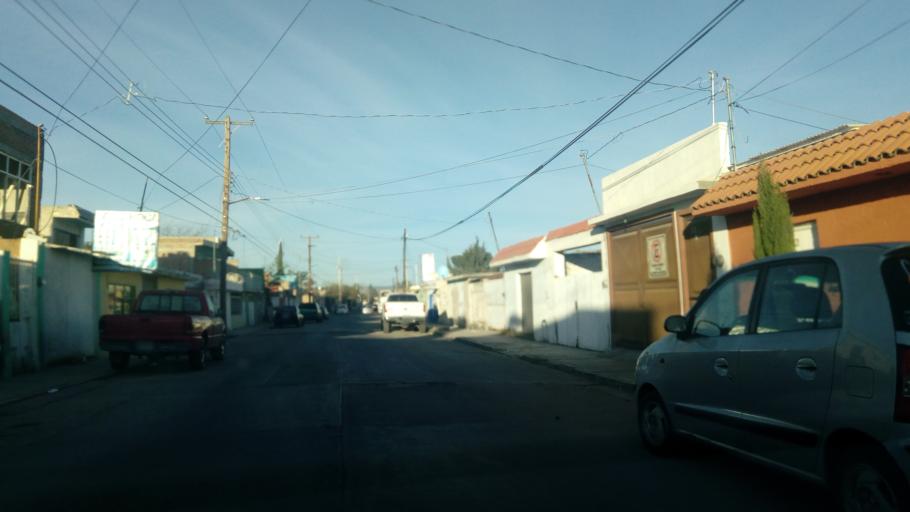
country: MX
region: Durango
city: Victoria de Durango
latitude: 24.0026
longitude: -104.6565
